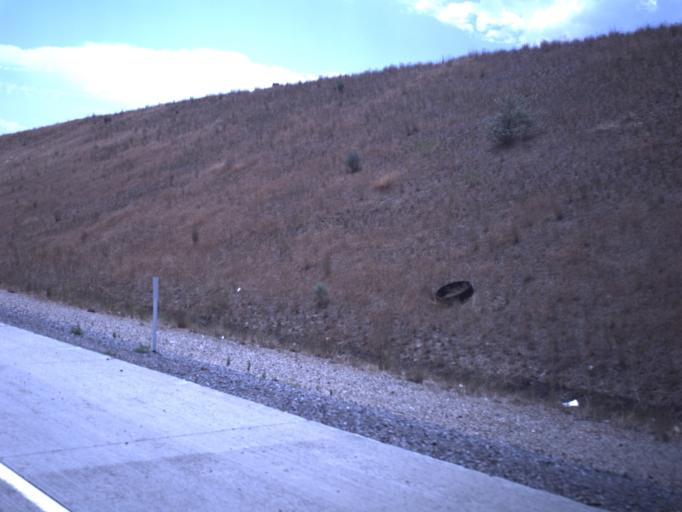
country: US
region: Utah
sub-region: Salt Lake County
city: Oquirrh
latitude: 40.6162
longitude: -112.0406
